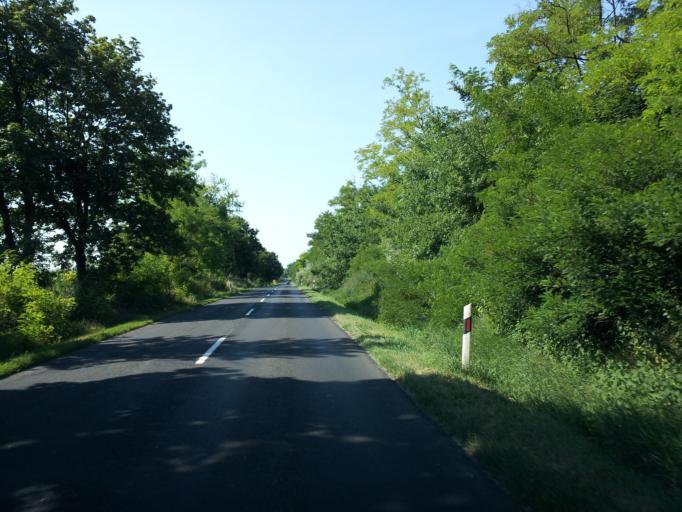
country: HU
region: Fejer
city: Lovasbereny
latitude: 47.3459
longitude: 18.5788
